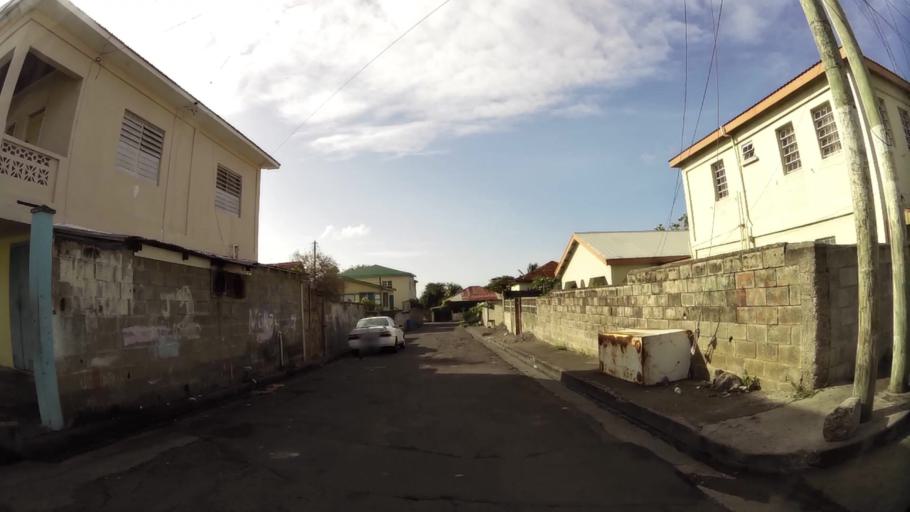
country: KN
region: Saint George Basseterre
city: Basseterre
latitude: 17.2926
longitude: -62.7360
